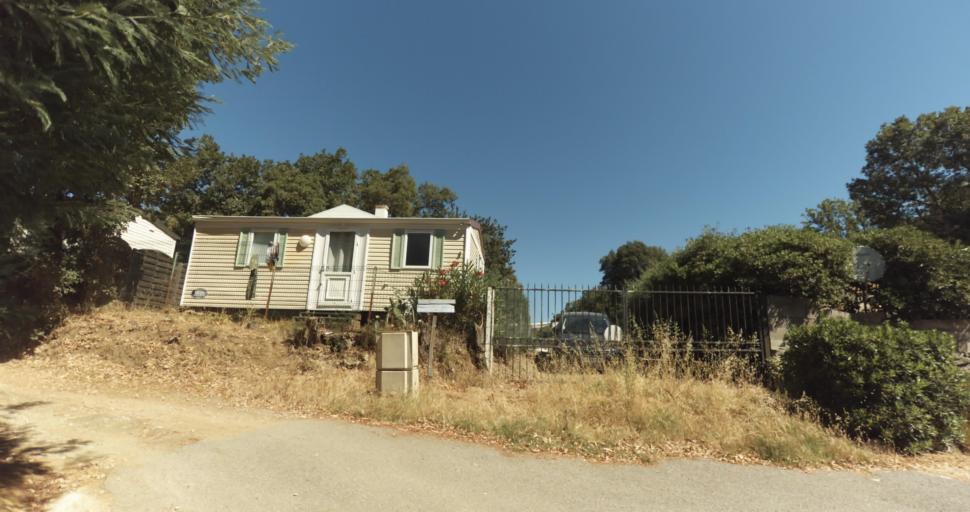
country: FR
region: Provence-Alpes-Cote d'Azur
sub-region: Departement du Var
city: Gassin
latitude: 43.2388
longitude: 6.5786
